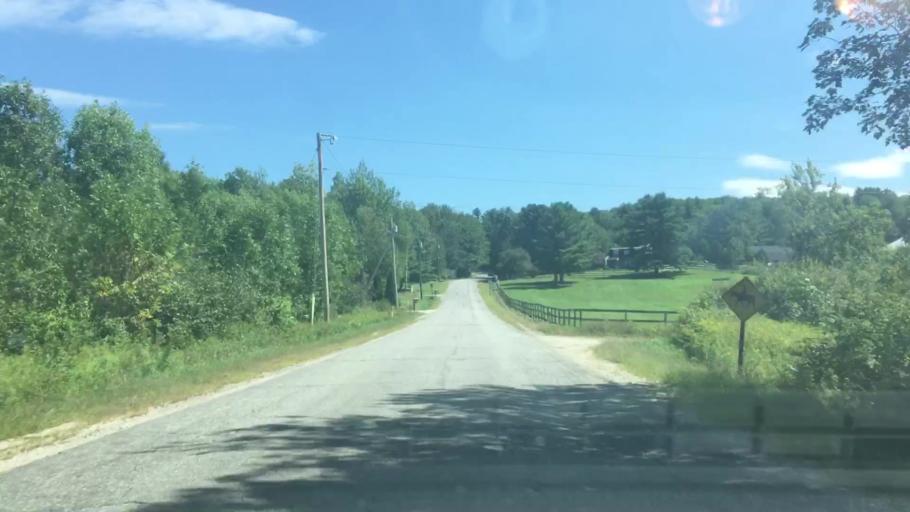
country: US
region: Maine
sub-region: Androscoggin County
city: Sabattus
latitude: 44.1228
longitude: -70.0630
